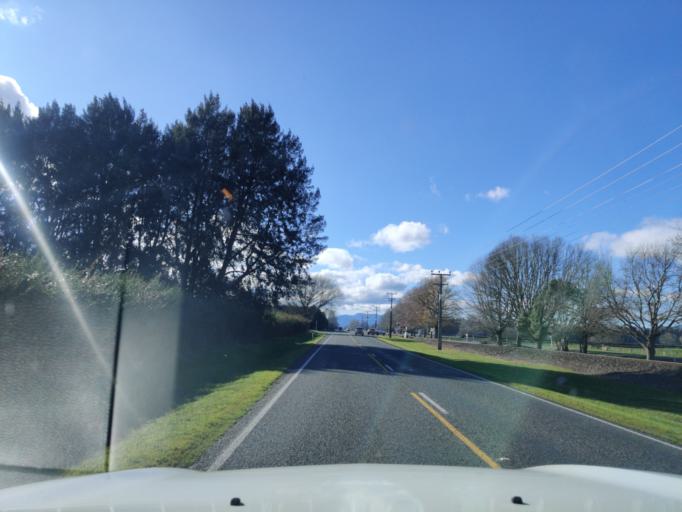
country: NZ
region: Waikato
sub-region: Matamata-Piako District
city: Matamata
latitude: -37.8541
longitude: 175.7577
